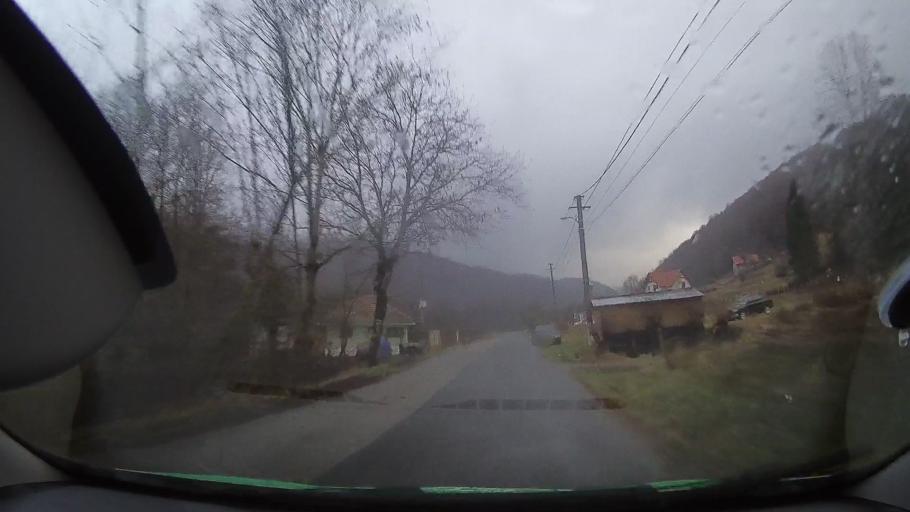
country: RO
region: Hunedoara
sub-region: Comuna Ribita
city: Ribita
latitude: 46.2579
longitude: 22.7463
